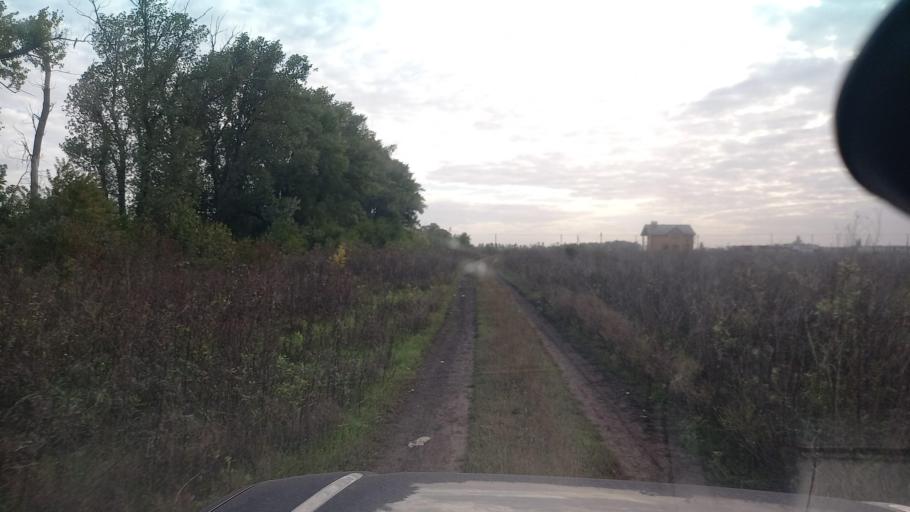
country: RU
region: Krasnodarskiy
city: Krasnodar
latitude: 45.1336
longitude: 38.9192
